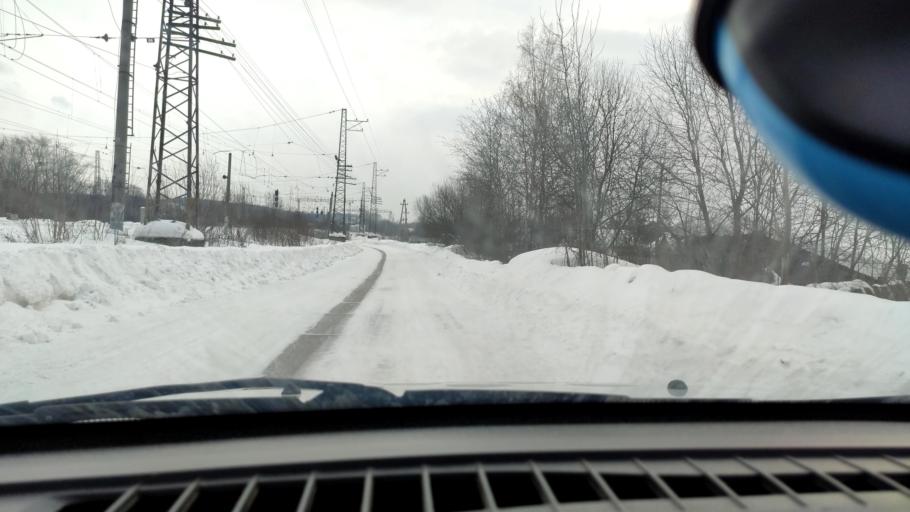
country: RU
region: Perm
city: Overyata
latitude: 58.0836
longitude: 55.8700
